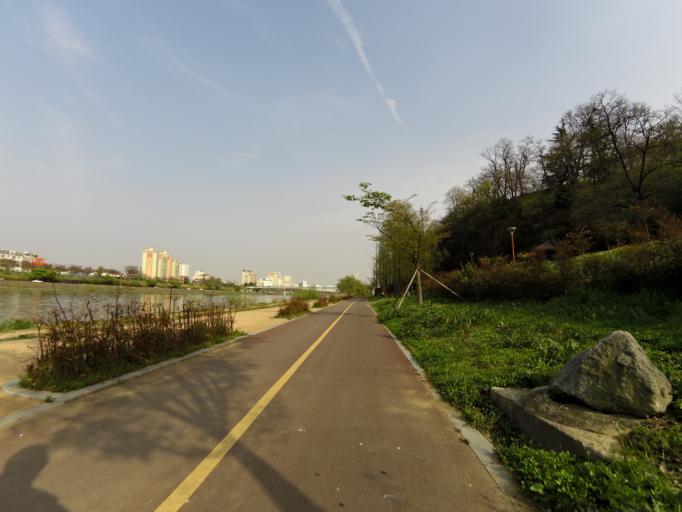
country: KR
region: Daegu
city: Daegu
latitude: 35.8869
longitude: 128.6437
